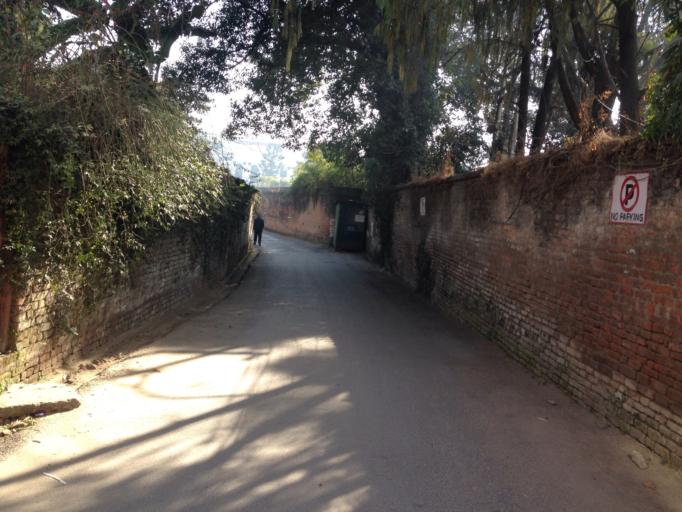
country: NP
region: Central Region
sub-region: Bagmati Zone
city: Kathmandu
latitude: 27.7194
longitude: 85.3183
